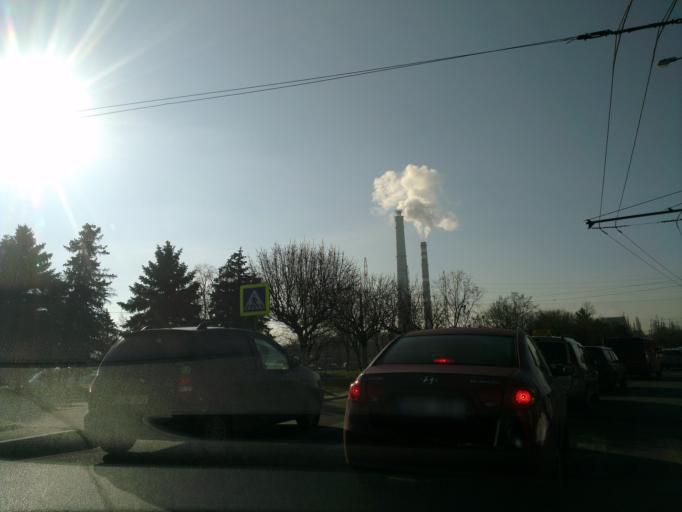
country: MD
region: Chisinau
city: Chisinau
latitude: 47.0358
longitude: 28.8890
